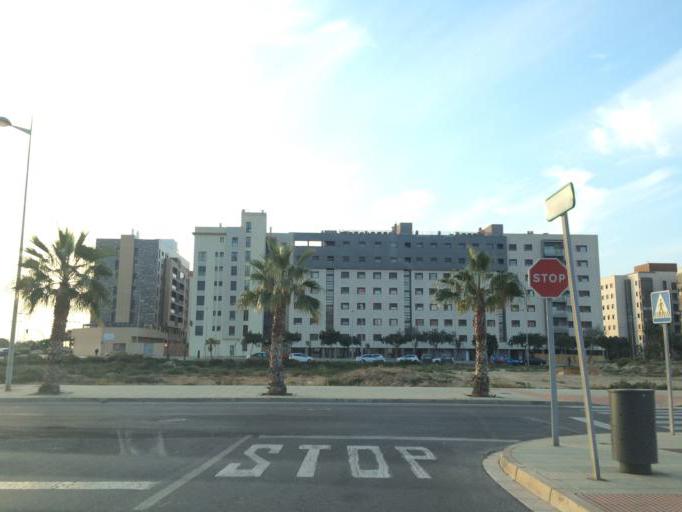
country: ES
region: Andalusia
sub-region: Provincia de Almeria
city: Almeria
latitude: 36.8334
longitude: -2.4392
